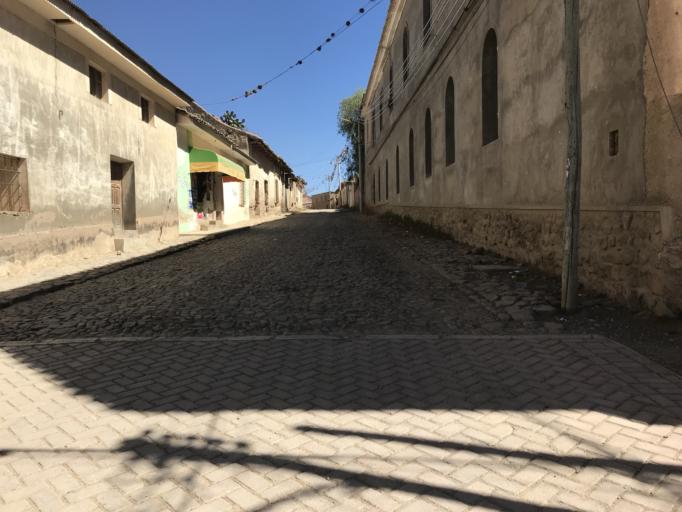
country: BO
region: Cochabamba
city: Tarata
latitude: -17.6157
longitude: -66.0295
